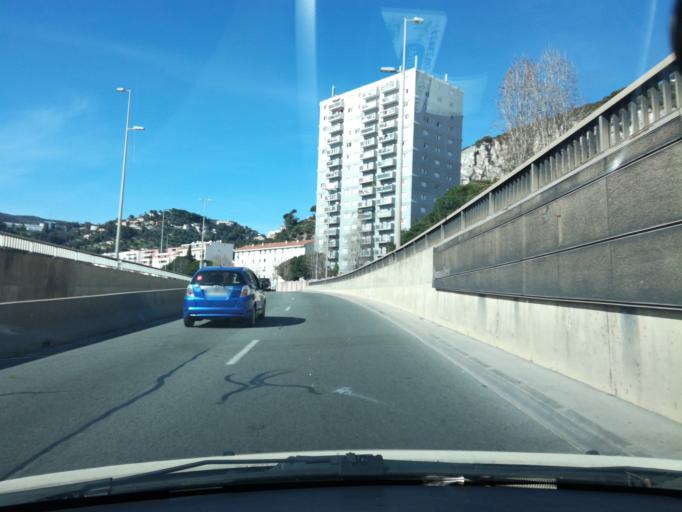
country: FR
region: Provence-Alpes-Cote d'Azur
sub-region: Departement des Alpes-Maritimes
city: Saint-Andre-de-la-Roche
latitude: 43.7237
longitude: 7.2885
